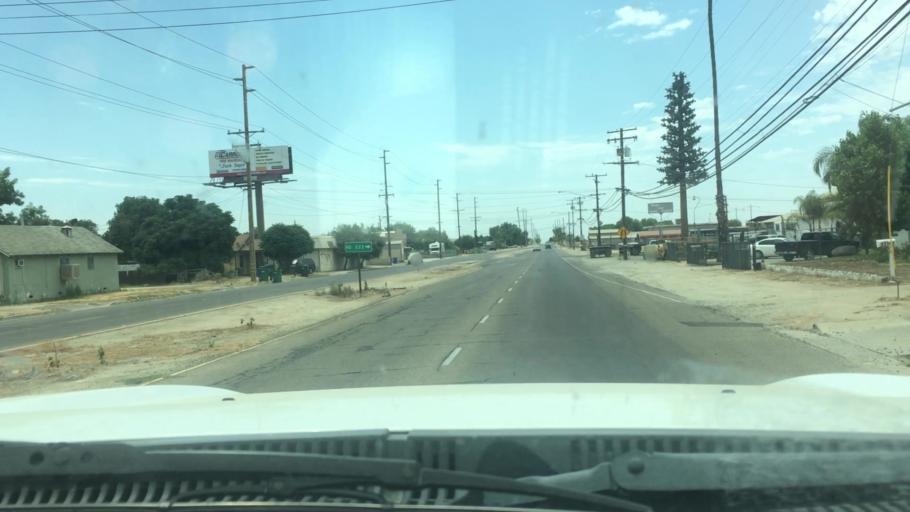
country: US
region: California
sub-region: Tulare County
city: Porterville
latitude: 36.0659
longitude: -119.0738
